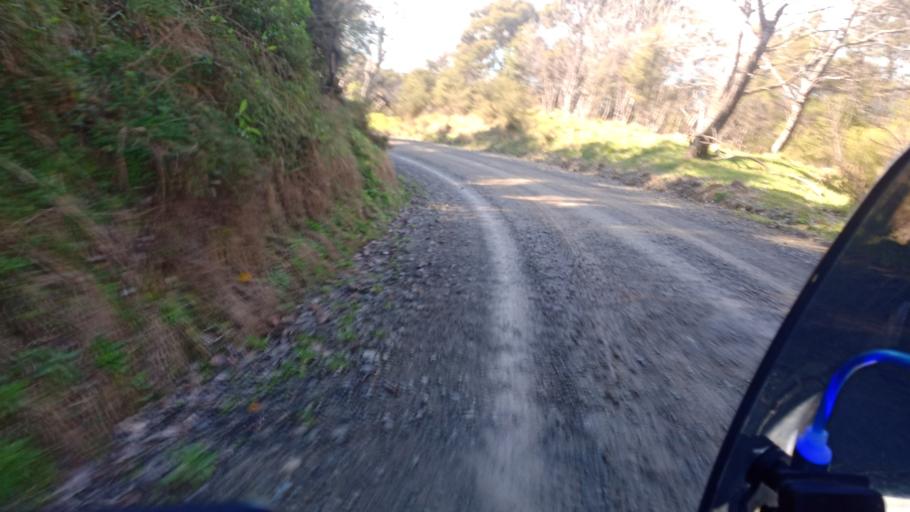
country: NZ
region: Gisborne
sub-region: Gisborne District
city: Gisborne
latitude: -38.2245
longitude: 178.3145
